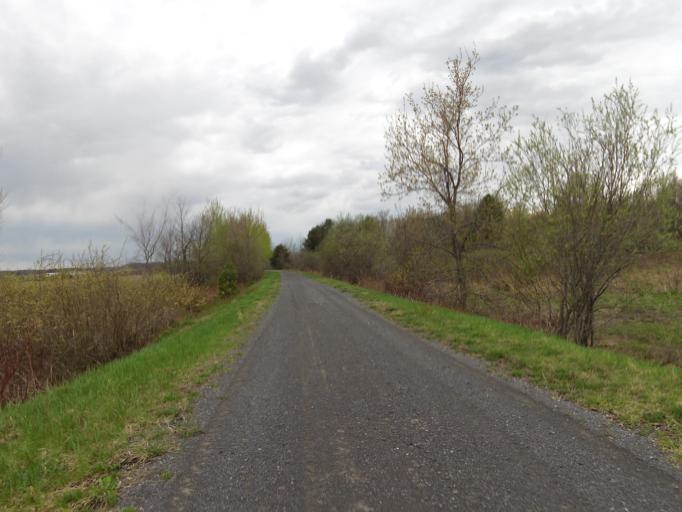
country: CA
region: Quebec
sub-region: Outaouais
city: Papineauville
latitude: 45.5196
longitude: -74.9705
